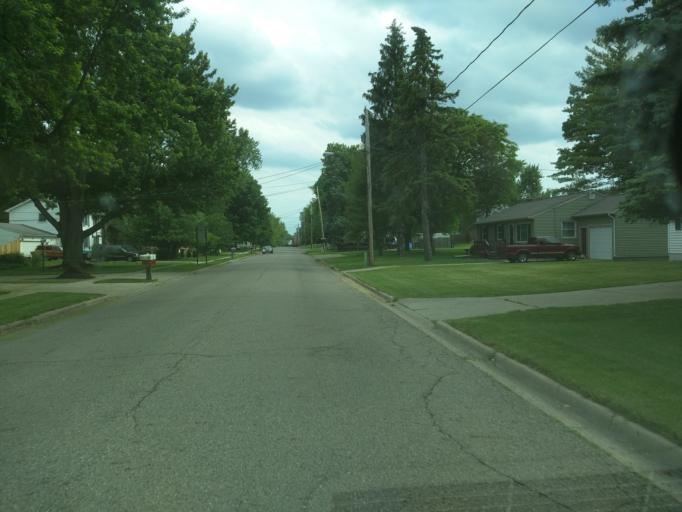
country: US
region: Michigan
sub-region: Eaton County
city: Waverly
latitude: 42.7460
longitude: -84.6134
